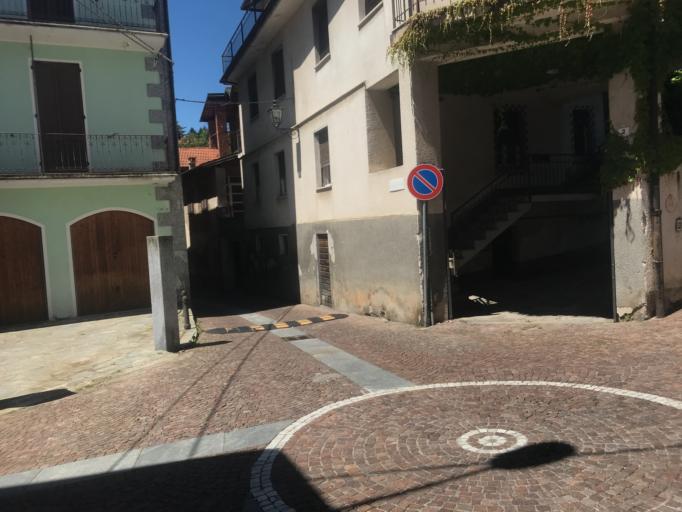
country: IT
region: Piedmont
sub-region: Provincia di Novara
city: Colazza
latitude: 45.7917
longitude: 8.4983
